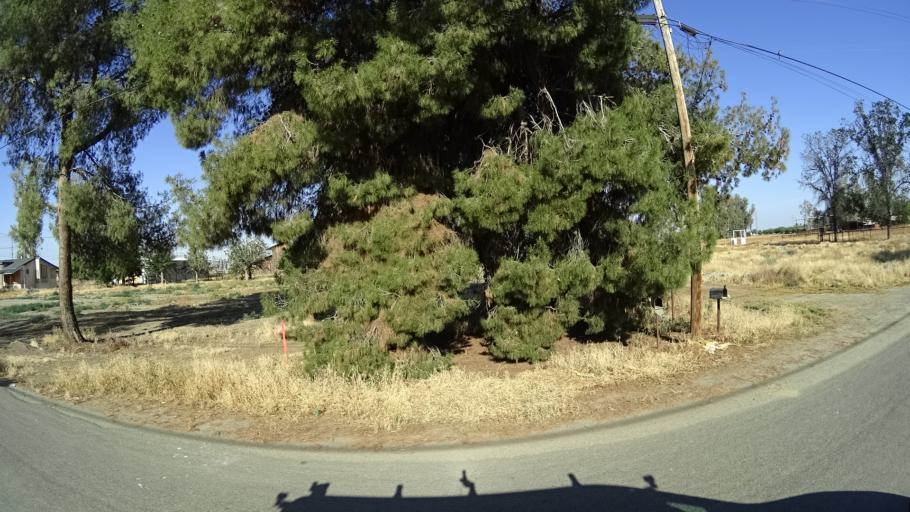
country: US
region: California
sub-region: Kings County
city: Corcoran
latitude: 36.1107
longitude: -119.5541
